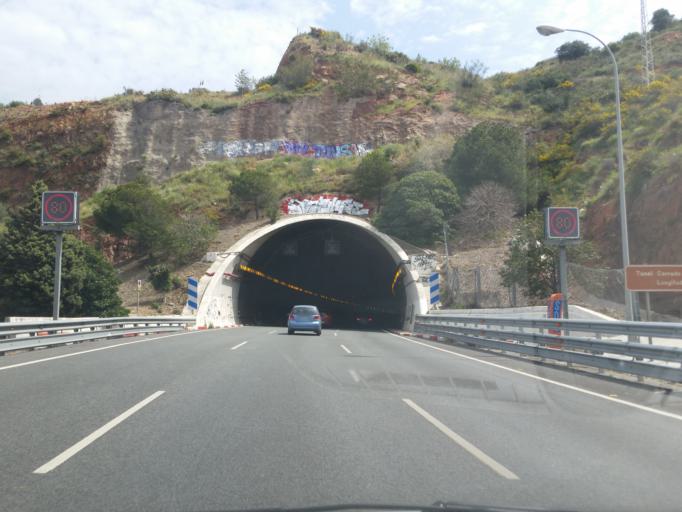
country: ES
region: Andalusia
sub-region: Provincia de Malaga
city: Malaga
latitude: 36.7403
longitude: -4.3858
